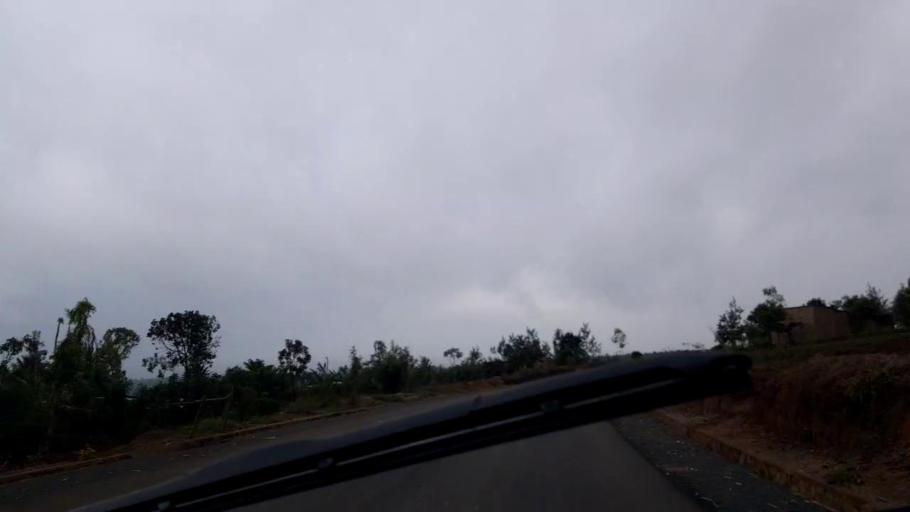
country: RW
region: Northern Province
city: Byumba
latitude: -1.4238
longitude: 30.2693
